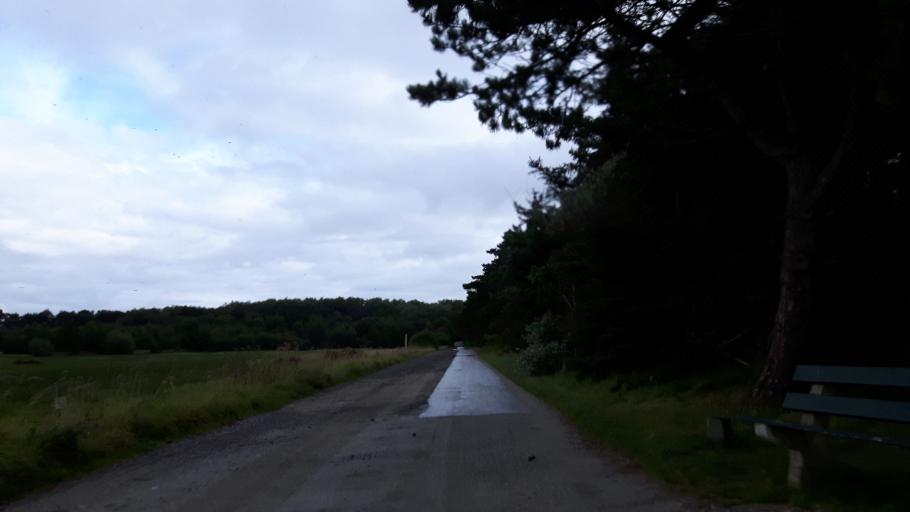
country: NL
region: Friesland
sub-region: Gemeente Ameland
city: Nes
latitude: 53.4504
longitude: 5.7572
